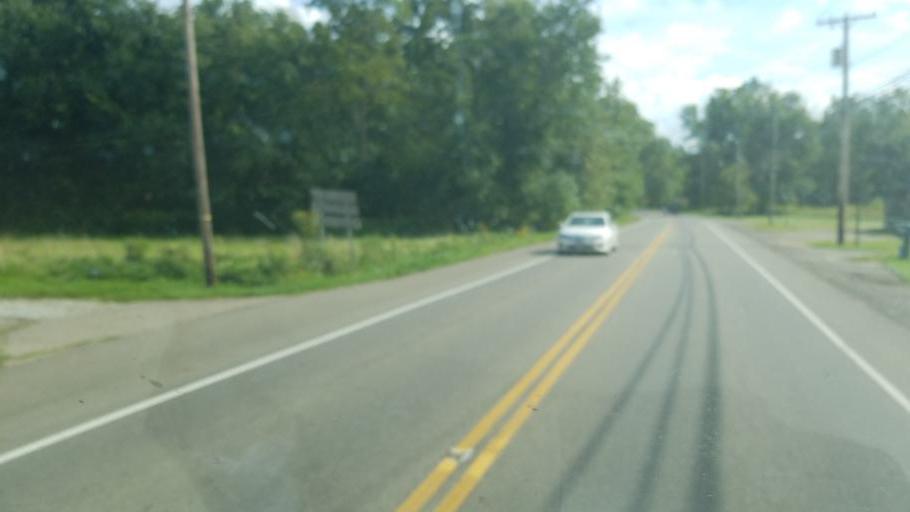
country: US
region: Ohio
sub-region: Carroll County
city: Lake Mohawk
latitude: 40.6754
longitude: -81.2610
